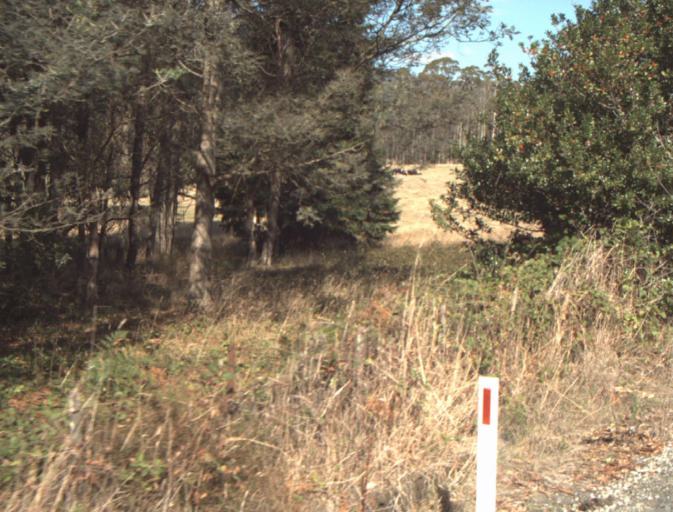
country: AU
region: Tasmania
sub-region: Launceston
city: Mayfield
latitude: -41.2313
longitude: 147.2354
